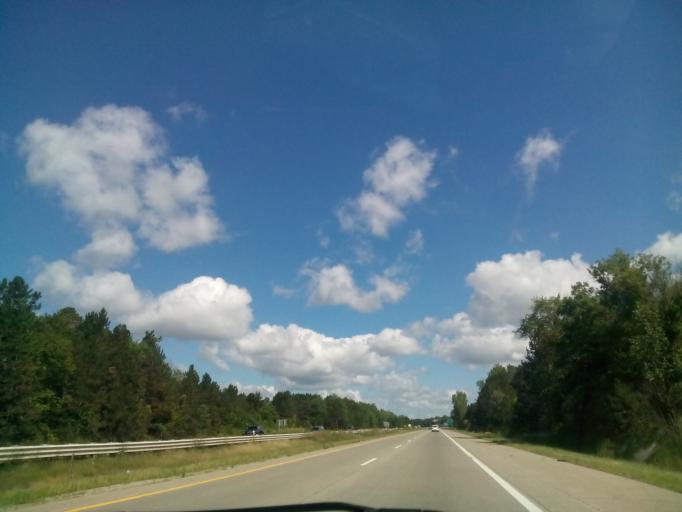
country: US
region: Michigan
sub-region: Genesee County
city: Lake Fenton
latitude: 42.9244
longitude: -83.7254
